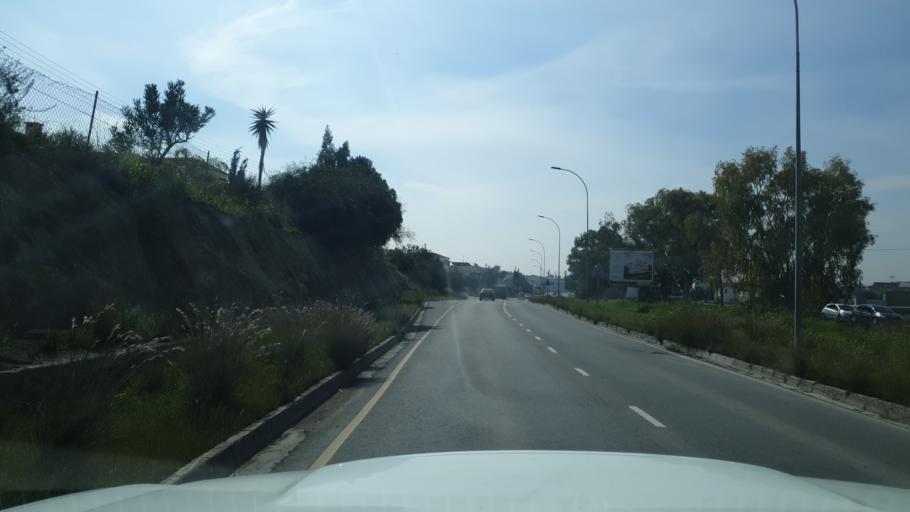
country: CY
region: Lefkosia
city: Kato Deftera
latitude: 35.1370
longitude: 33.3010
